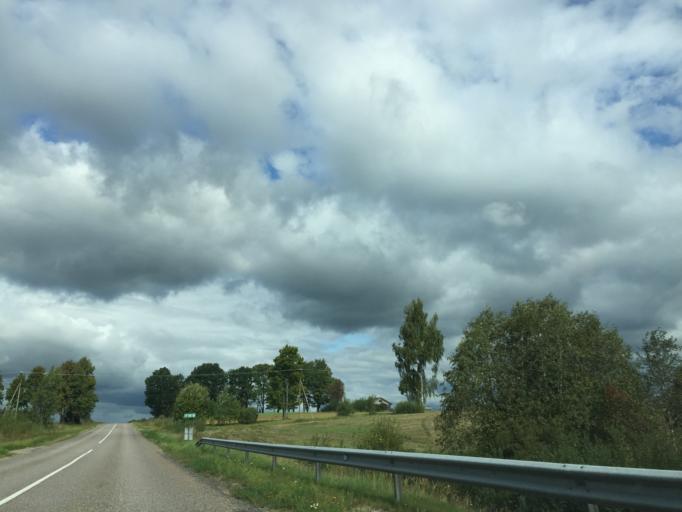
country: LV
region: Pargaujas
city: Stalbe
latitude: 57.4568
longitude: 24.9147
